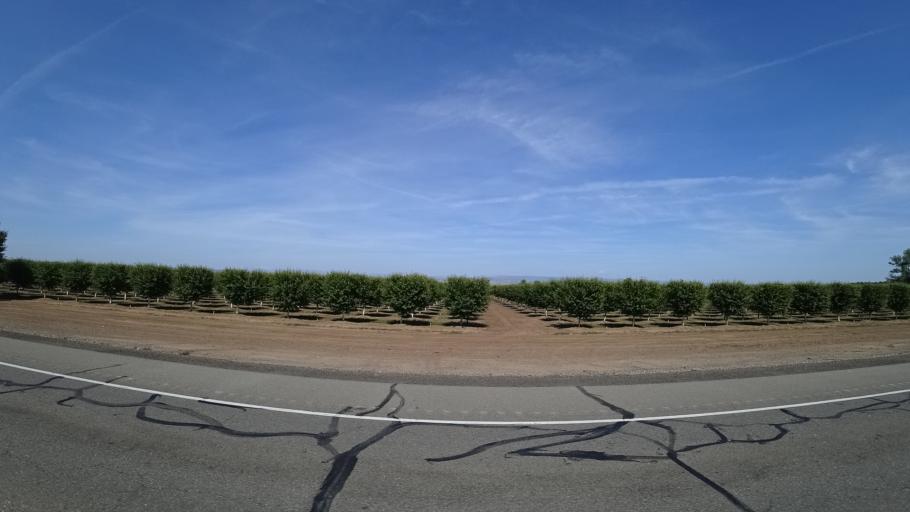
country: US
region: California
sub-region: Tehama County
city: Los Molinos
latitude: 39.9652
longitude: -122.0713
